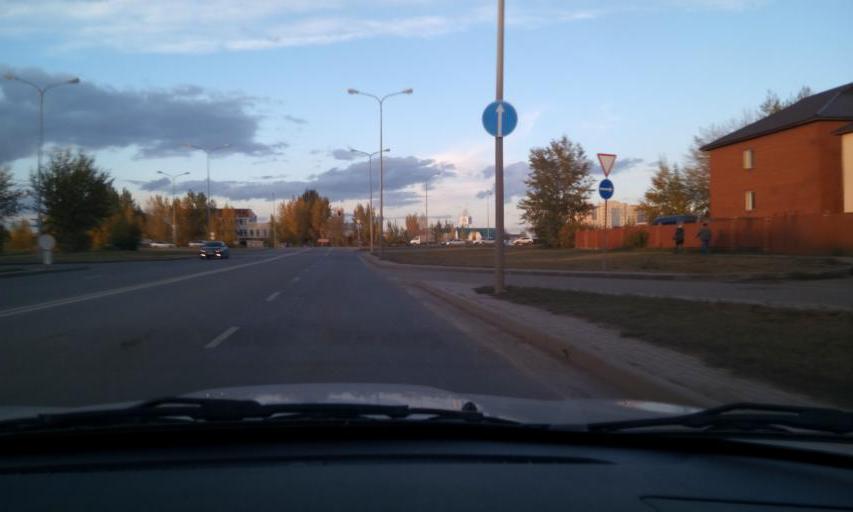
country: KZ
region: Astana Qalasy
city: Astana
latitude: 51.1396
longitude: 71.5207
